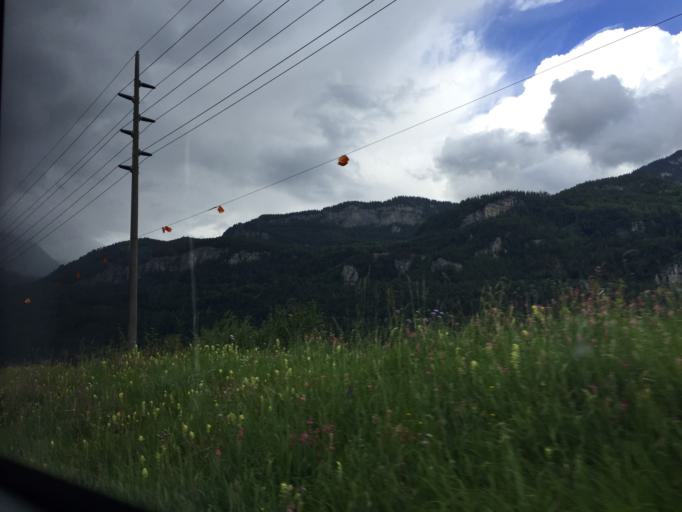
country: CH
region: Bern
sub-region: Interlaken-Oberhasli District
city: Meiringen
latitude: 46.7327
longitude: 8.1612
